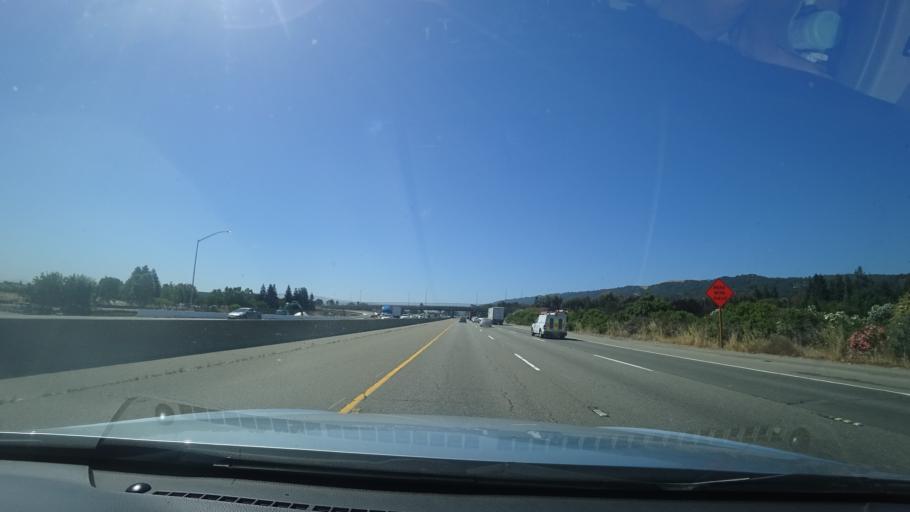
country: US
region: California
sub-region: Alameda County
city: Dublin
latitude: 37.6927
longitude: -121.9195
